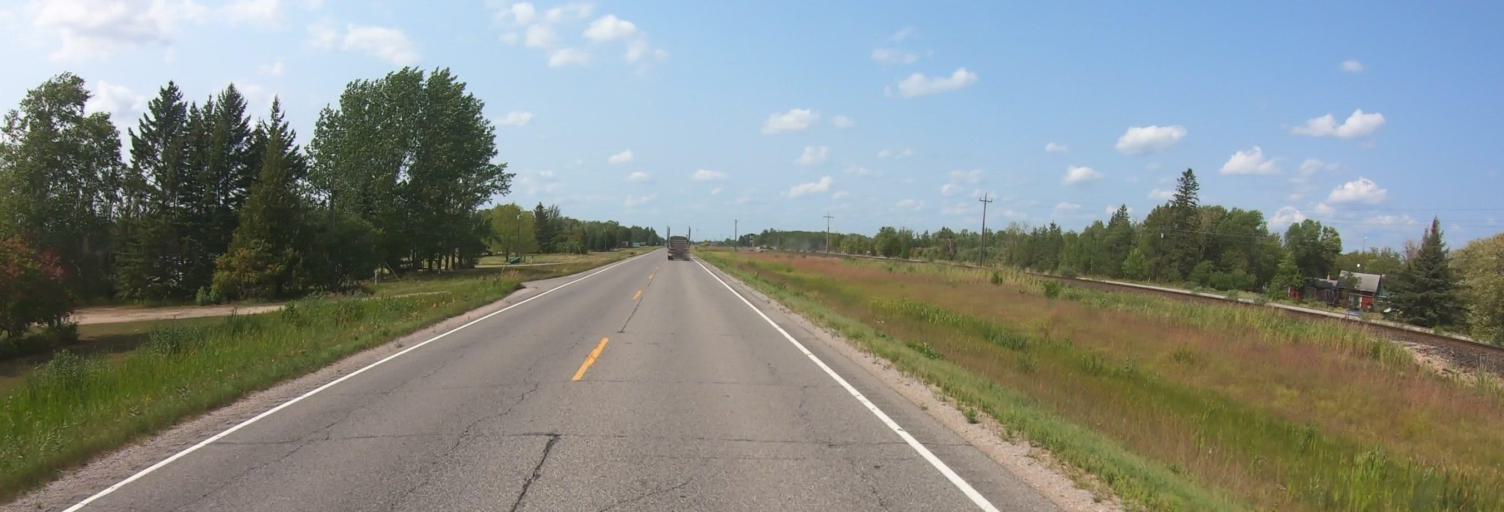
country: US
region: Minnesota
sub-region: Roseau County
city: Warroad
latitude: 48.8853
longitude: -95.2954
